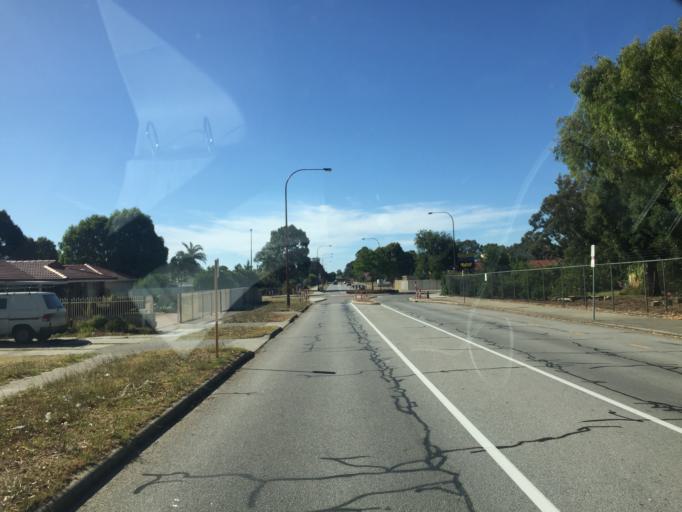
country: AU
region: Western Australia
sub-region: Gosnells
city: Maddington
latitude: -32.0559
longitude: 116.0031
